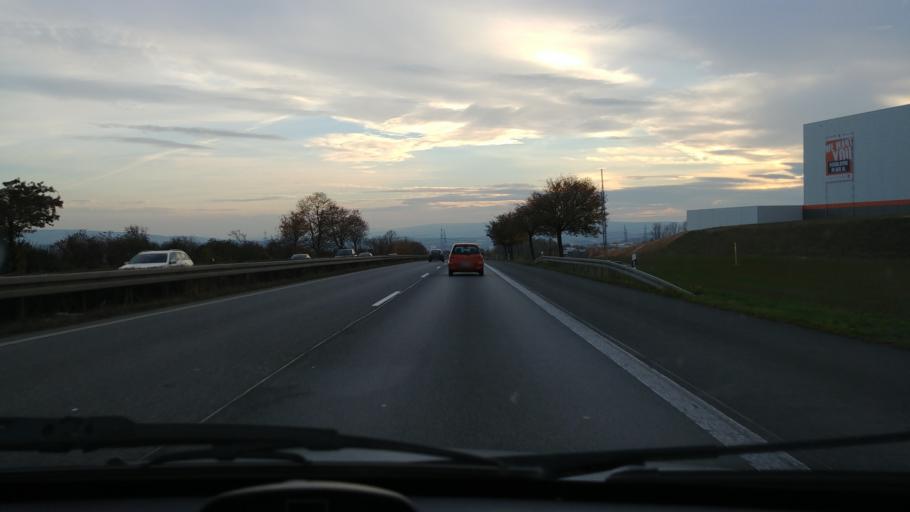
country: DE
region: Hesse
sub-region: Regierungsbezirk Giessen
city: Dehrn
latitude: 50.4144
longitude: 8.0796
